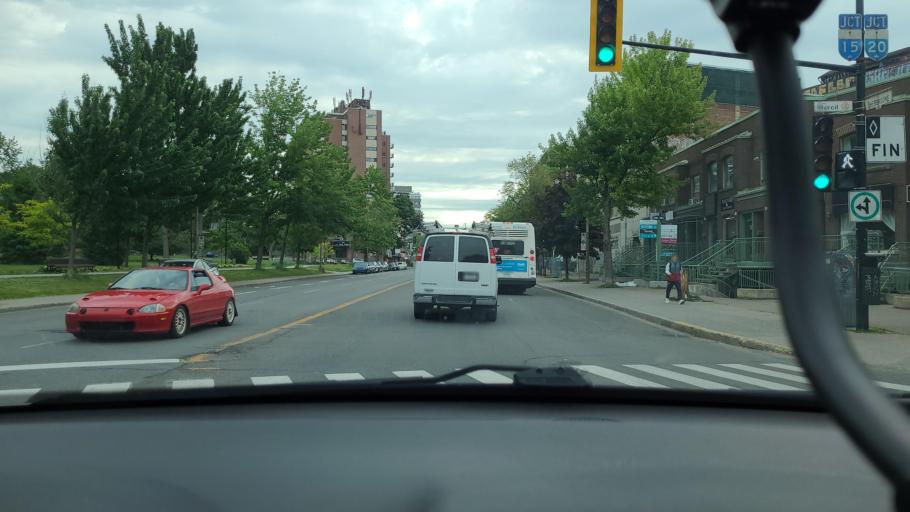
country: CA
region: Quebec
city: Saint-Raymond
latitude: 45.4716
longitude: -73.6138
